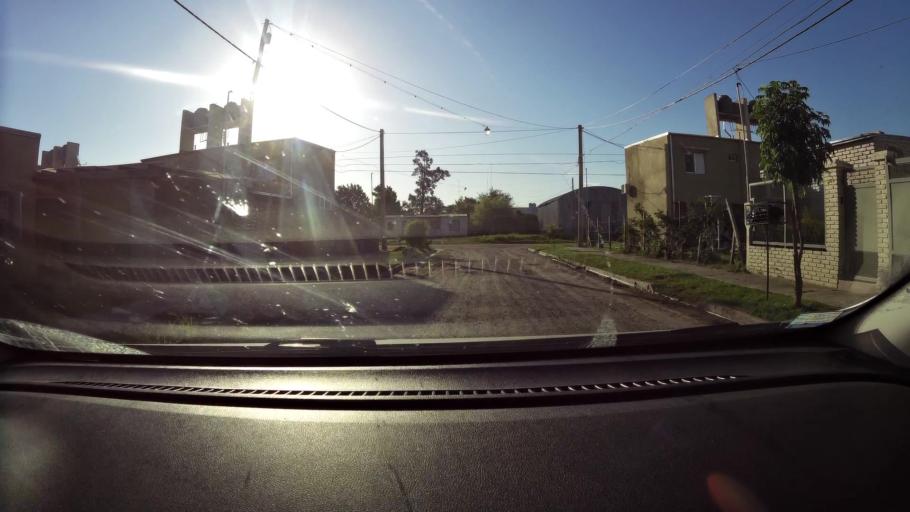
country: AR
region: Santa Fe
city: Santa Fe de la Vera Cruz
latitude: -31.5898
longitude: -60.6897
